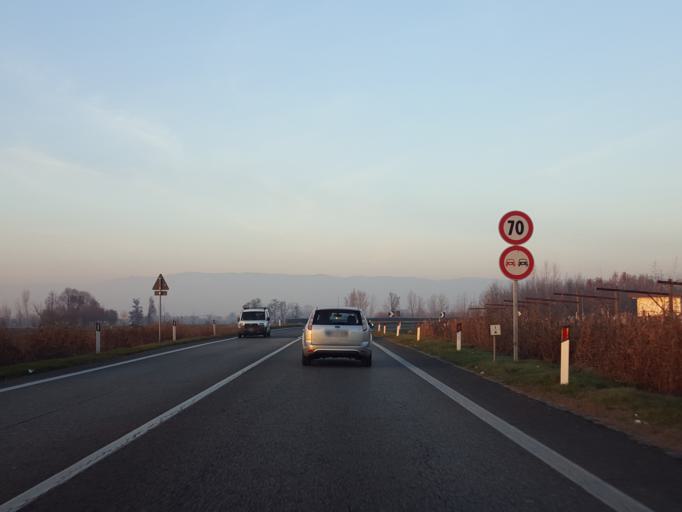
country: IT
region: Veneto
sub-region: Provincia di Vicenza
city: Lisiera
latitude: 45.5759
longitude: 11.5883
